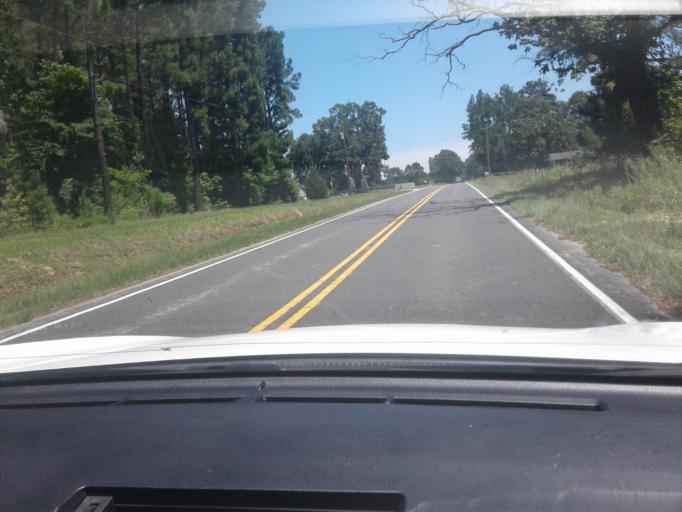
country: US
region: North Carolina
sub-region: Harnett County
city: Lillington
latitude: 35.3894
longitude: -78.7807
